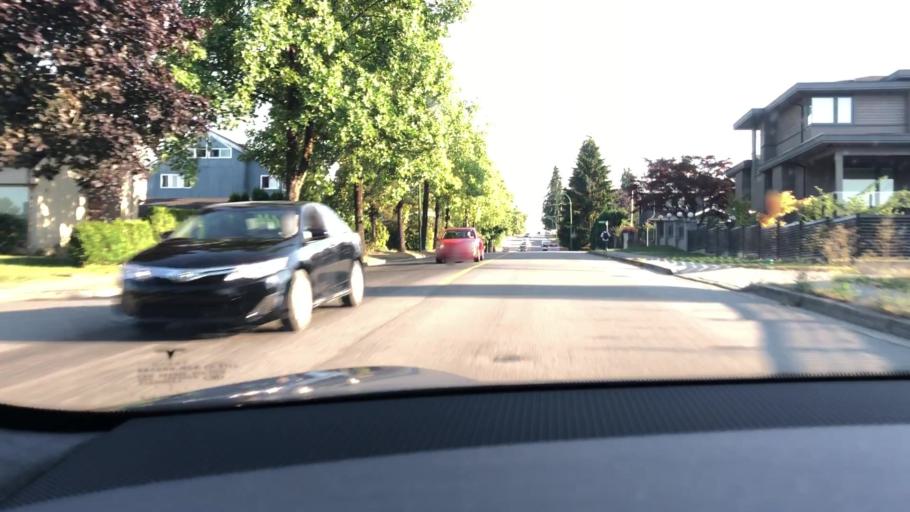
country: CA
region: British Columbia
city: Burnaby
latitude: 49.2283
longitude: -122.9719
